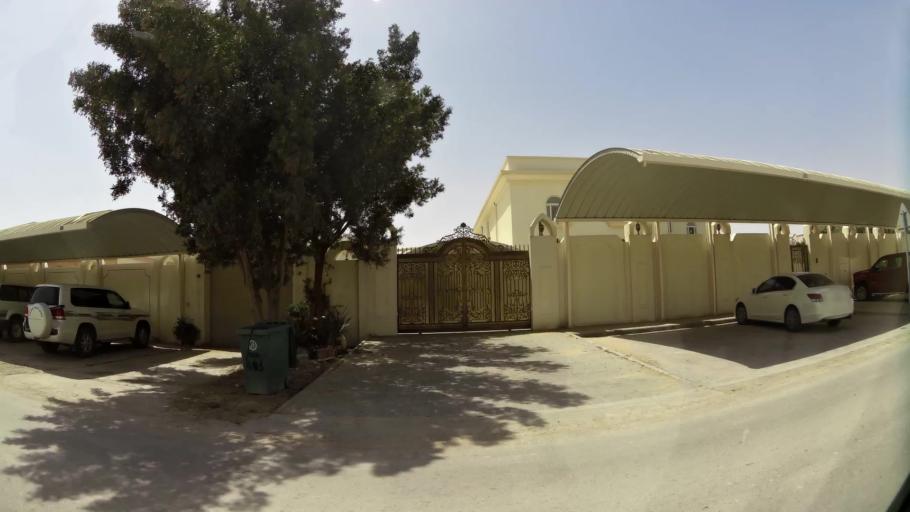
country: QA
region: Baladiyat Umm Salal
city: Umm Salal Muhammad
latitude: 25.3732
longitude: 51.4539
